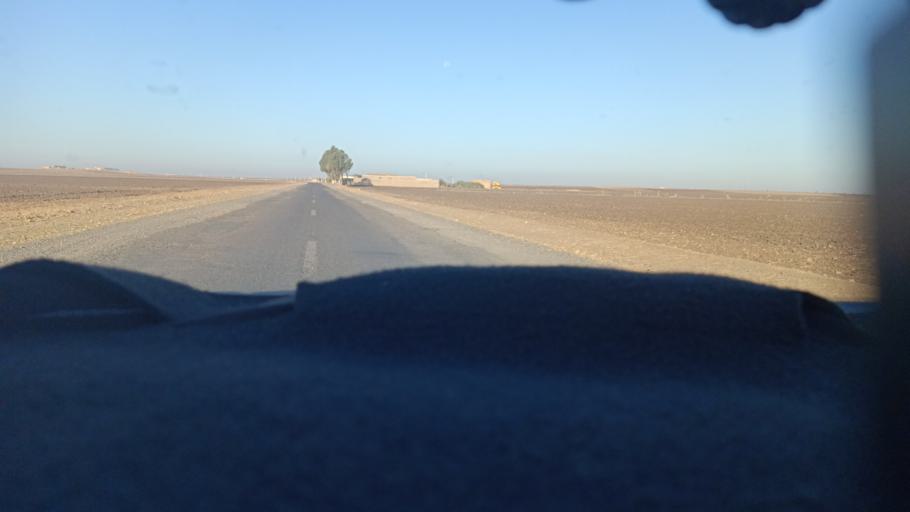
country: MA
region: Doukkala-Abda
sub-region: Safi
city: Youssoufia
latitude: 32.3714
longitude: -8.7137
